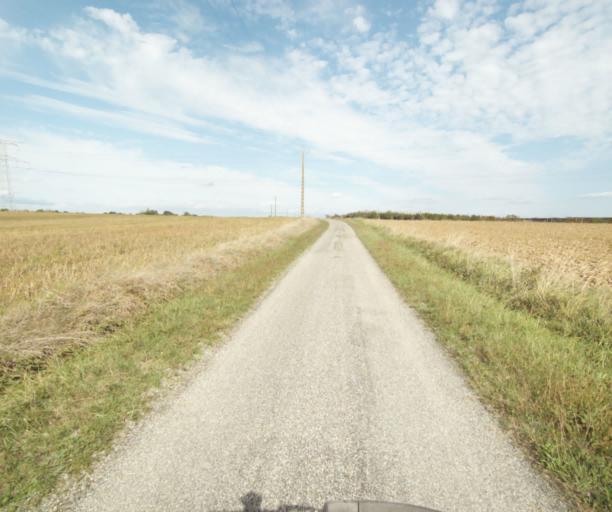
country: FR
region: Midi-Pyrenees
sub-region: Departement du Tarn-et-Garonne
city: Verdun-sur-Garonne
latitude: 43.8668
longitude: 1.1789
